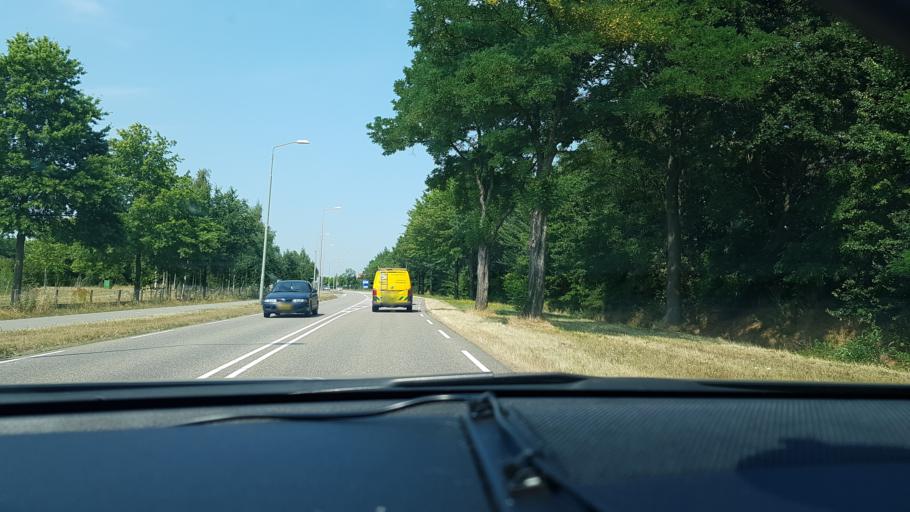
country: NL
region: Limburg
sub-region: Gemeente Roermond
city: Leeuwen
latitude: 51.1962
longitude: 6.0276
